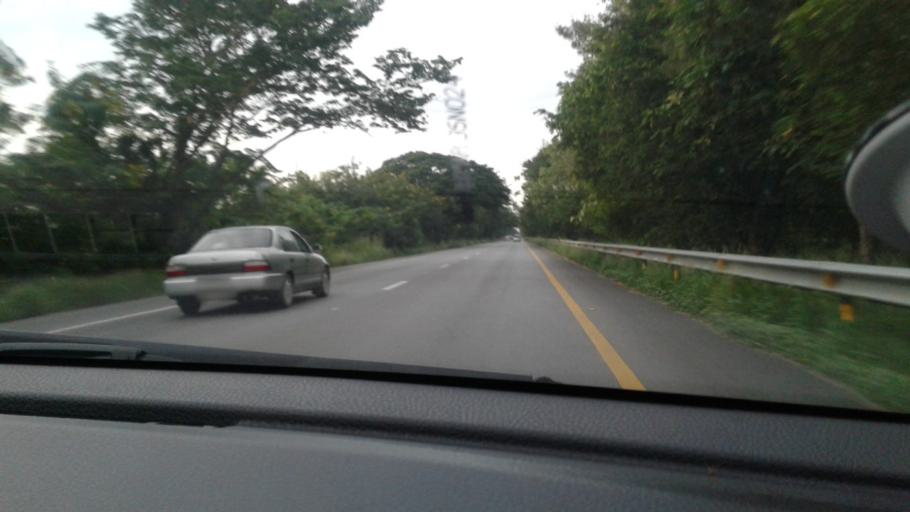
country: TH
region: Prachuap Khiri Khan
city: Hua Hin
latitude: 12.5010
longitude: 99.8868
